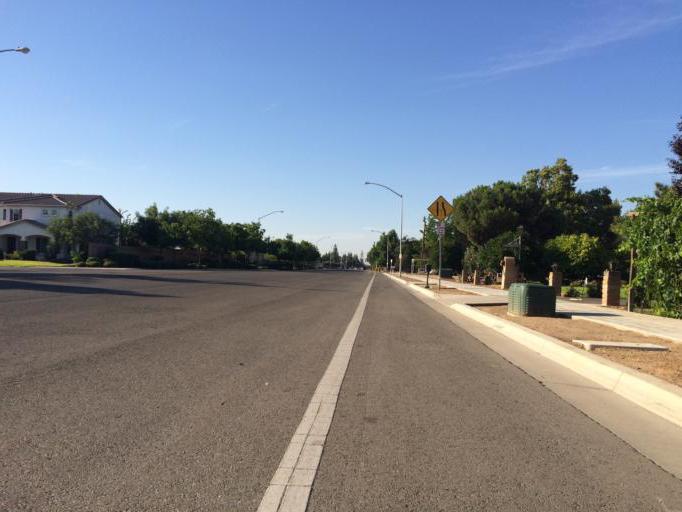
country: US
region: California
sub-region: Fresno County
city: Tarpey Village
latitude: 36.7902
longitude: -119.6730
